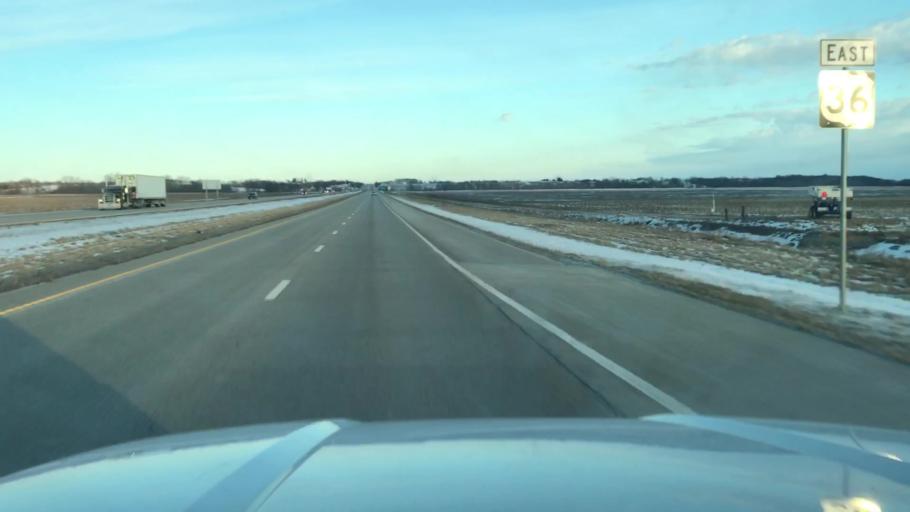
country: US
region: Missouri
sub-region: Buchanan County
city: Saint Joseph
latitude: 39.7479
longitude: -94.7455
